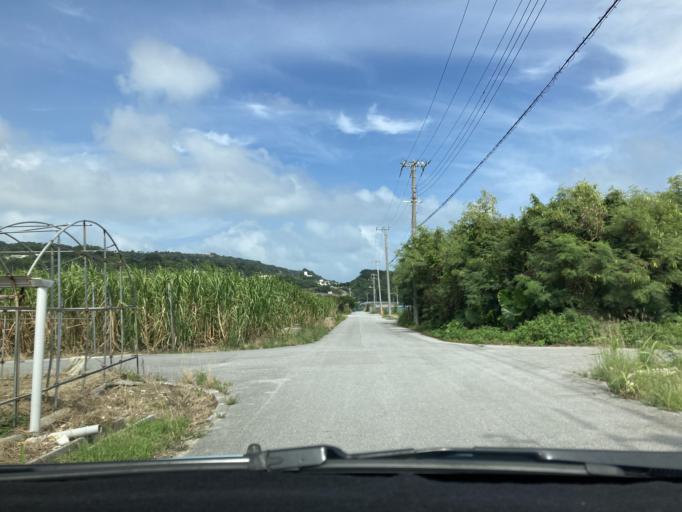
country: JP
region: Okinawa
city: Ginowan
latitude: 26.1513
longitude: 127.8058
